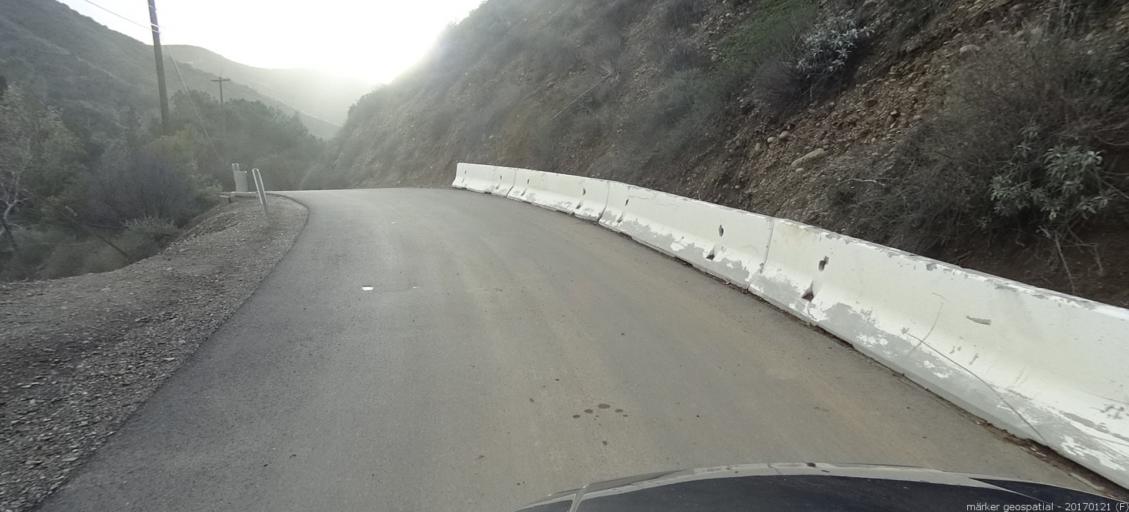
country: US
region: California
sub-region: Orange County
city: Portola Hills
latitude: 33.7105
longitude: -117.6219
